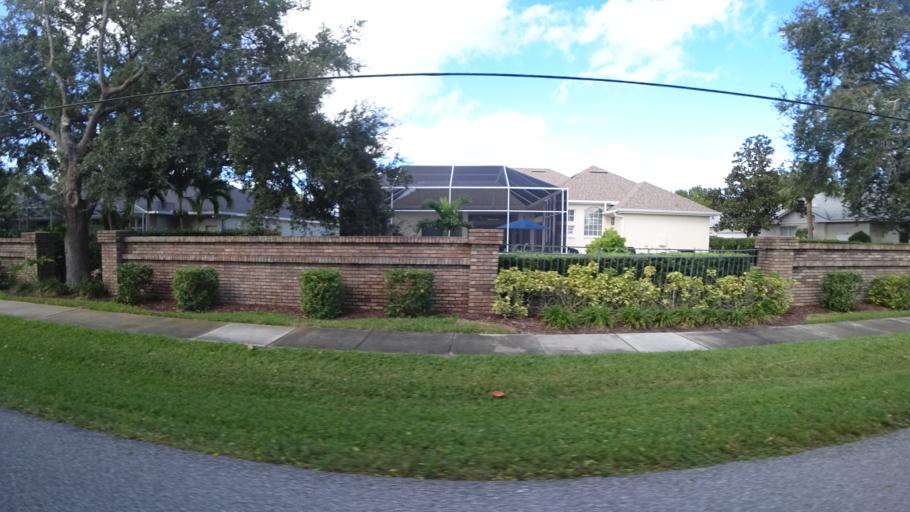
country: US
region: Florida
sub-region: Manatee County
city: West Bradenton
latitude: 27.5157
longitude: -82.6446
